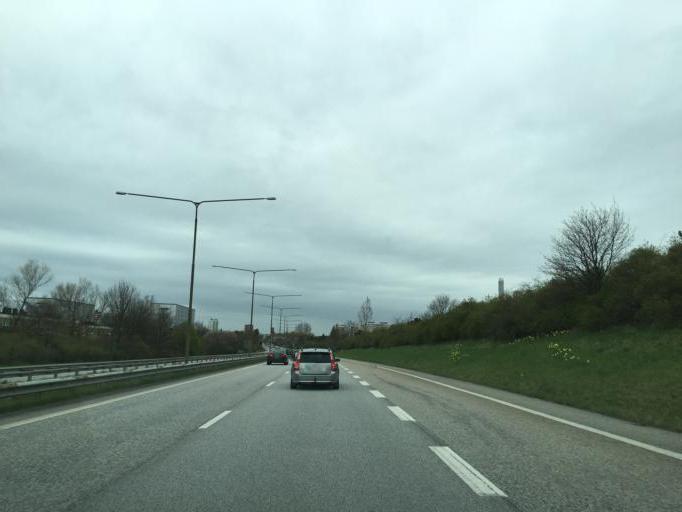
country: SE
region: Skane
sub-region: Malmo
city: Malmoe
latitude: 55.5696
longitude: 13.0039
